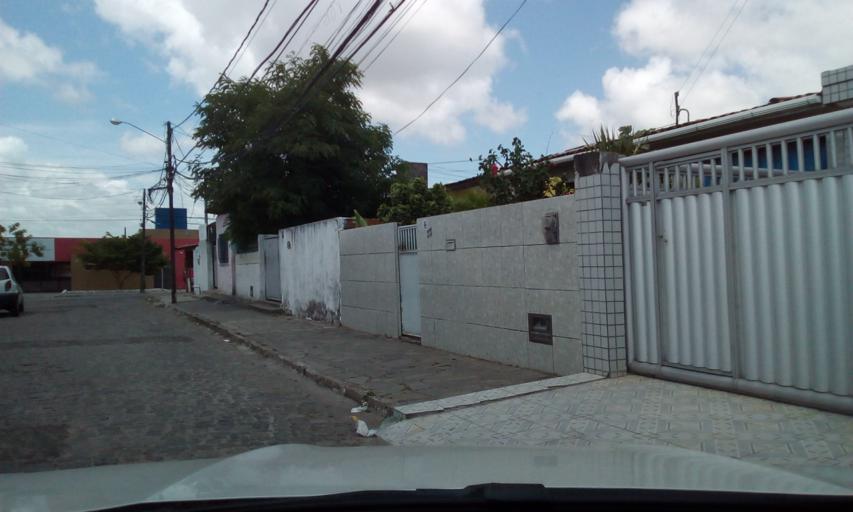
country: BR
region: Paraiba
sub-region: Joao Pessoa
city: Joao Pessoa
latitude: -7.1701
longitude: -34.8409
